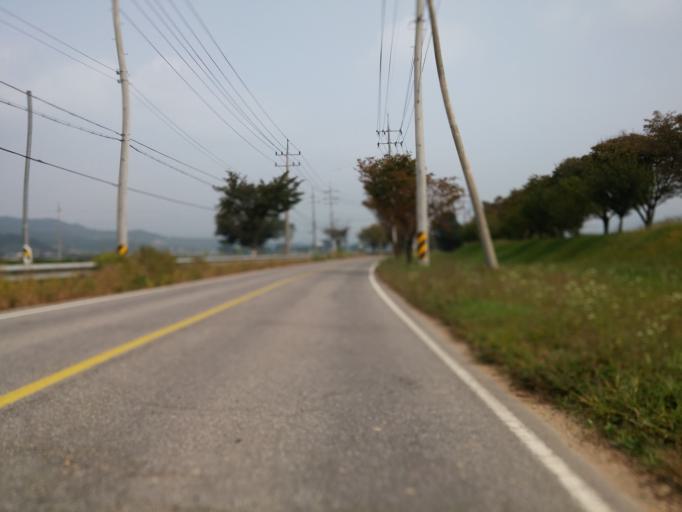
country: KR
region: Chungcheongbuk-do
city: Okcheon
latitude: 36.4241
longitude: 127.7793
